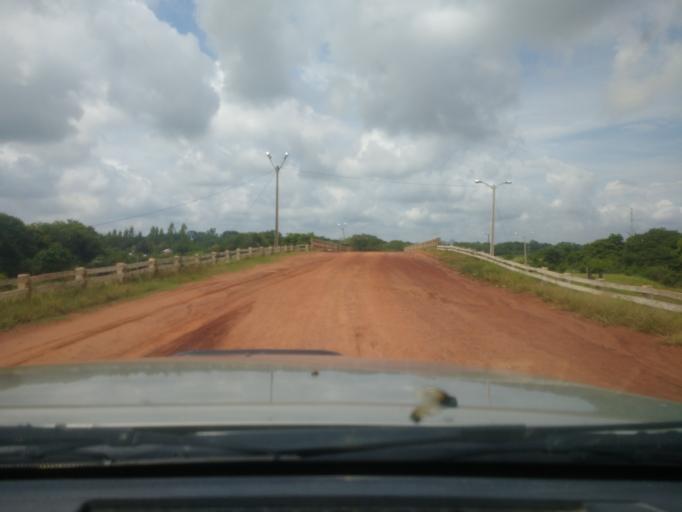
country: PY
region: San Pedro
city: Puerto Rosario
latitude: -24.4068
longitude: -57.1032
